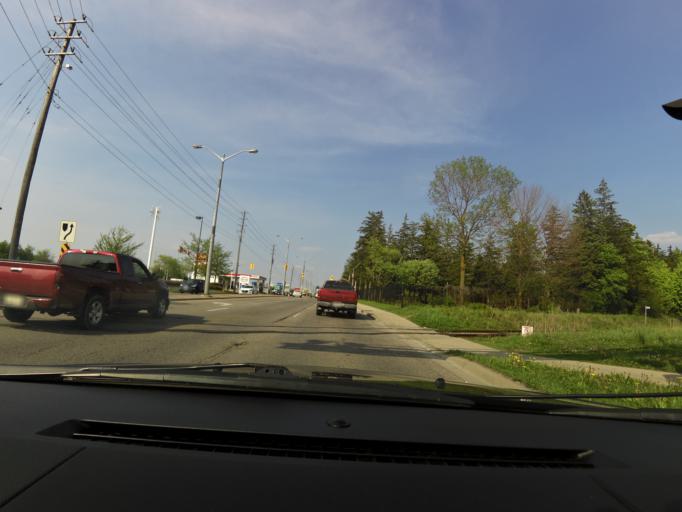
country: CA
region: Ontario
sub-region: Wellington County
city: Guelph
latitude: 43.5611
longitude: -80.2825
